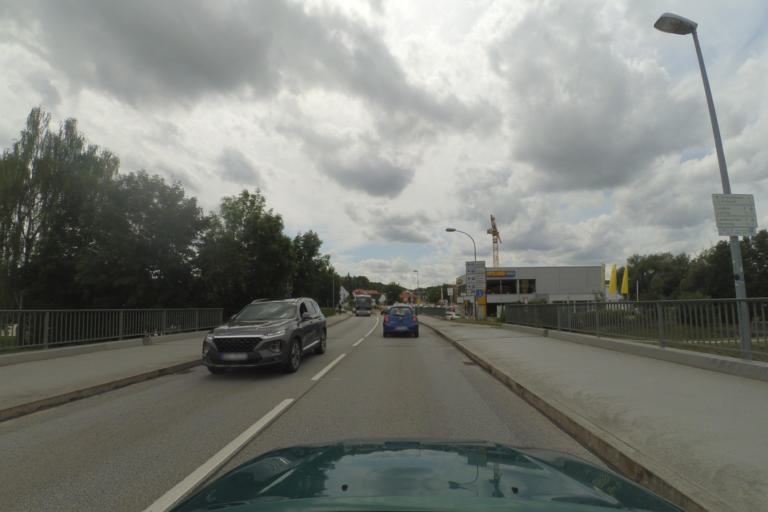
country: DE
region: Bavaria
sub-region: Lower Bavaria
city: Dingolfing
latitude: 48.6331
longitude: 12.4948
